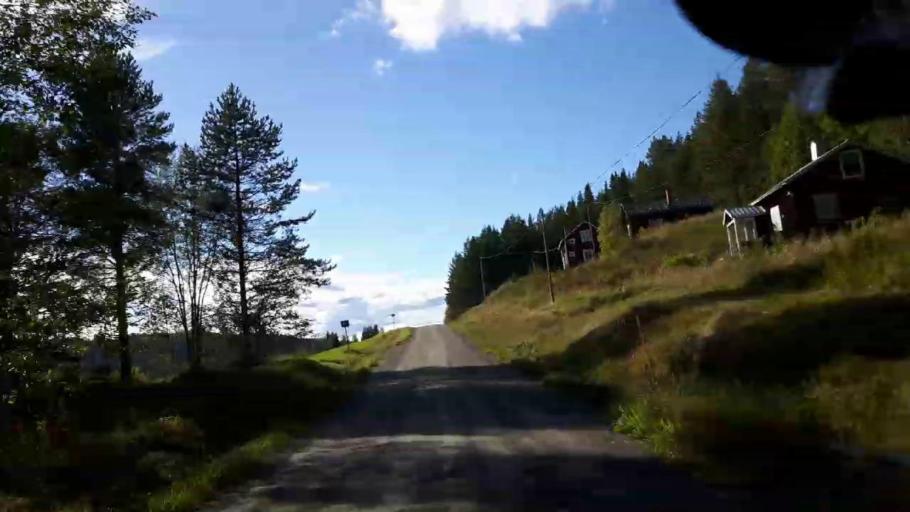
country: SE
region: Jaemtland
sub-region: Ragunda Kommun
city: Hammarstrand
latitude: 63.4761
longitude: 16.1609
